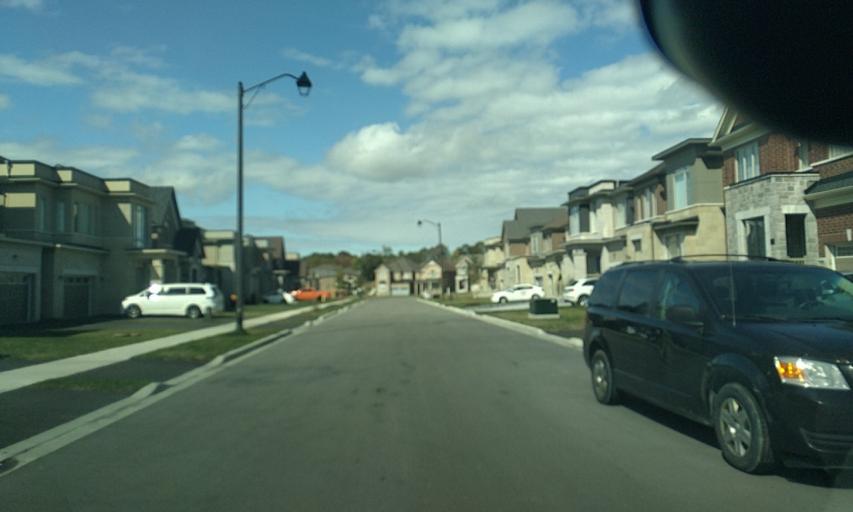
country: CA
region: Ontario
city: Newmarket
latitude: 44.0864
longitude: -79.4455
